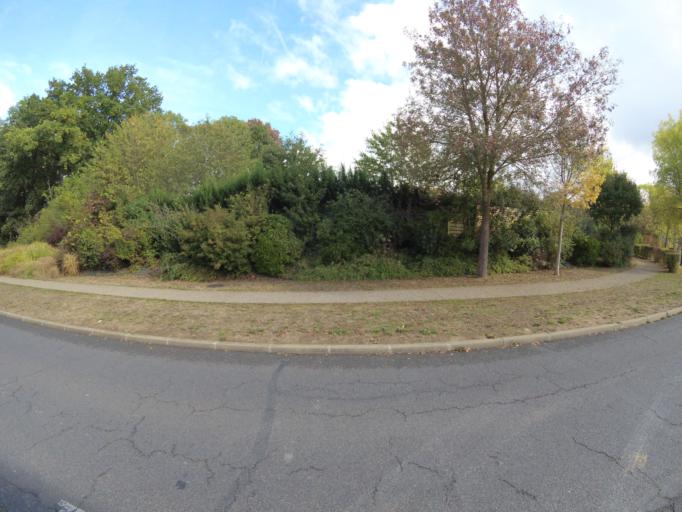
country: FR
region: Ile-de-France
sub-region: Departement de Seine-et-Marne
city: Montevrain
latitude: 48.8676
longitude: 2.7541
